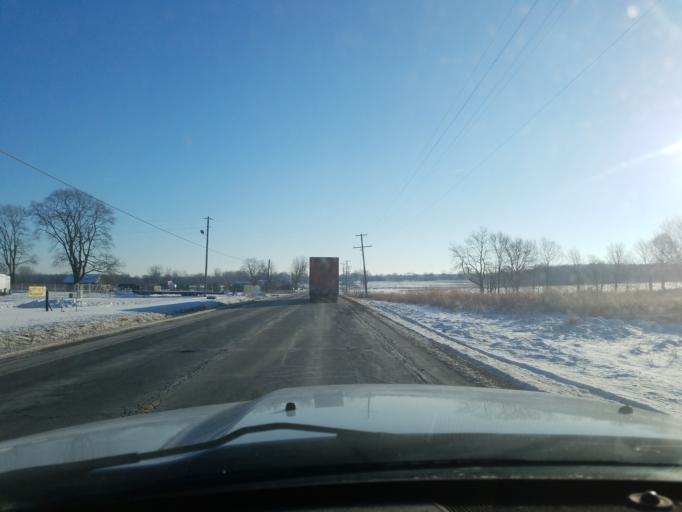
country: US
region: Indiana
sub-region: Noble County
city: Rome City
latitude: 41.4529
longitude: -85.3771
